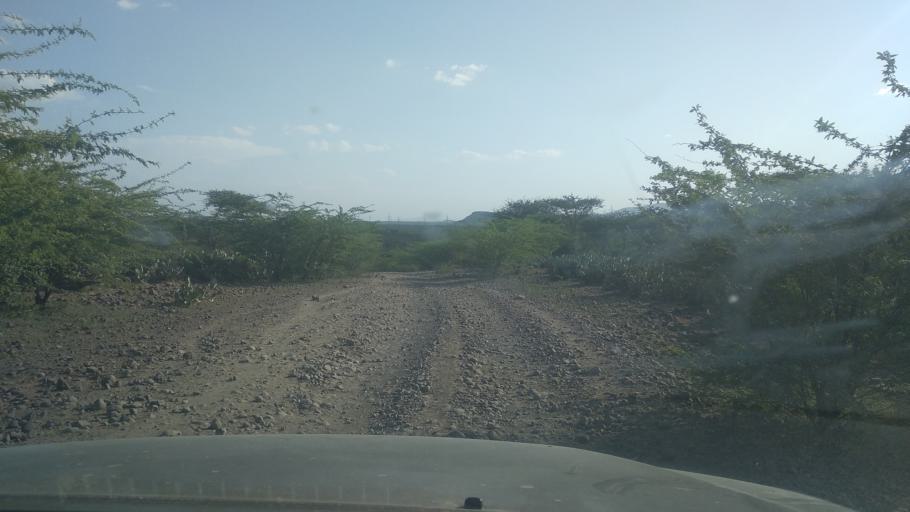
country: ET
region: Oromiya
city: Hirna
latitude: 9.4575
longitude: 40.9931
